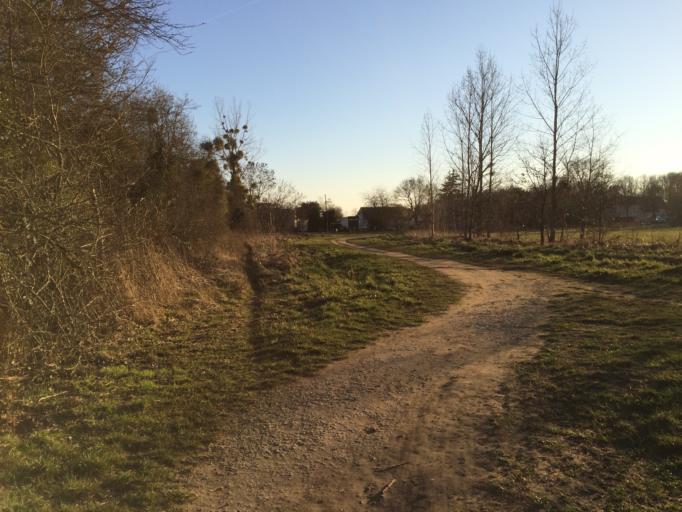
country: FR
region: Ile-de-France
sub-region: Departement de l'Essonne
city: Villebon-sur-Yvette
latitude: 48.7107
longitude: 2.2257
